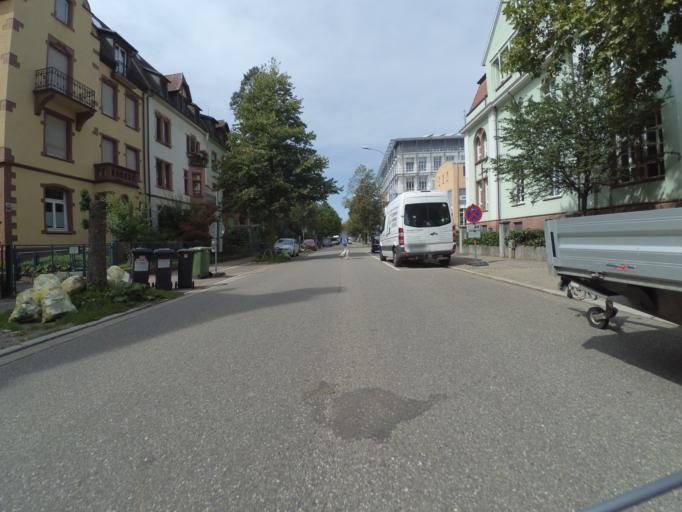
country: DE
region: Baden-Wuerttemberg
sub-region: Freiburg Region
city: Freiburg
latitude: 47.9917
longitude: 7.8613
